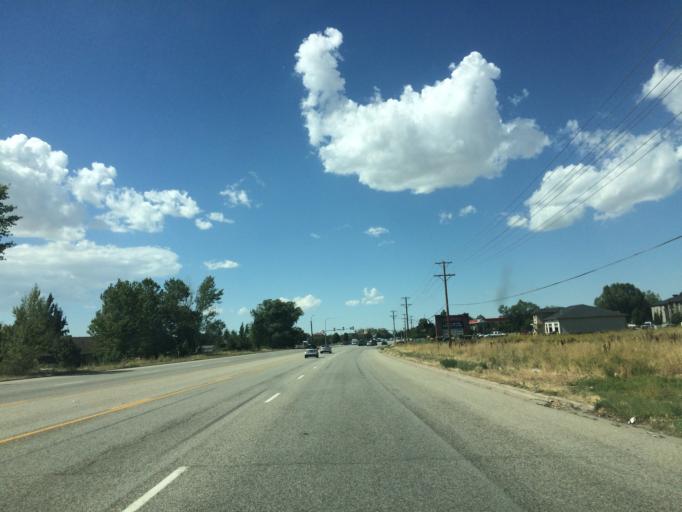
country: US
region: Utah
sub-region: Davis County
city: South Weber
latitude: 41.1015
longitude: -111.9360
